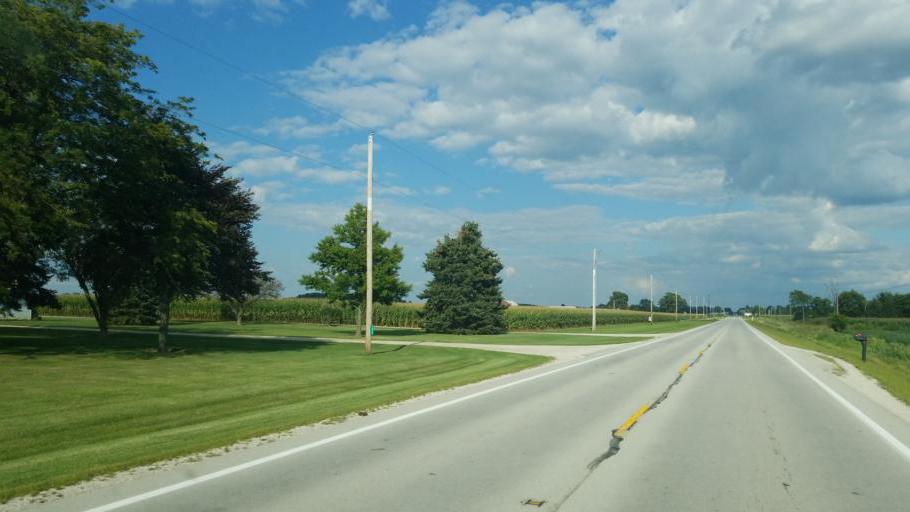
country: US
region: Ohio
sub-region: Sandusky County
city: Gibsonburg
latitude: 41.3413
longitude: -83.3972
